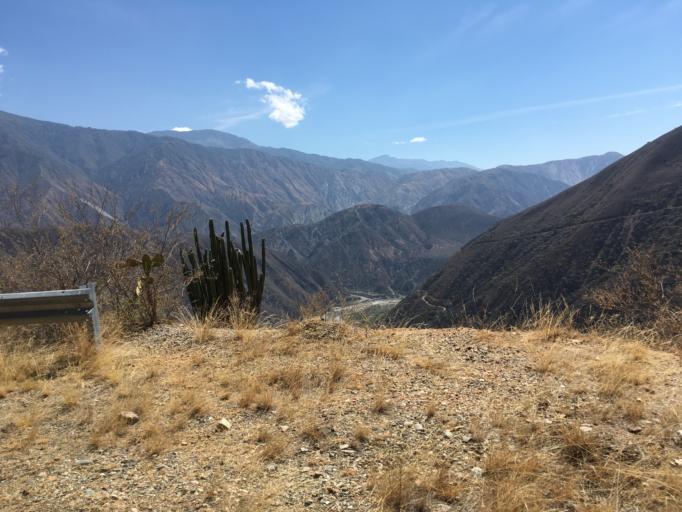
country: CO
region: Santander
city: Aratoca
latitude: 6.7797
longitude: -72.9935
